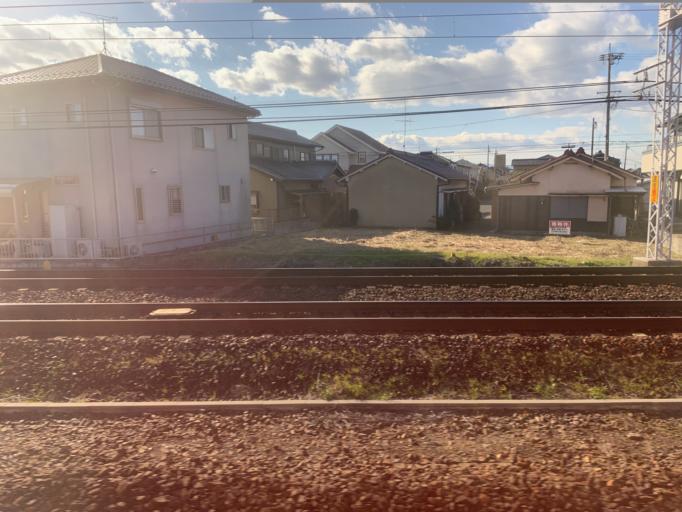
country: JP
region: Aichi
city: Ichinomiya
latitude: 35.3221
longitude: 136.7875
